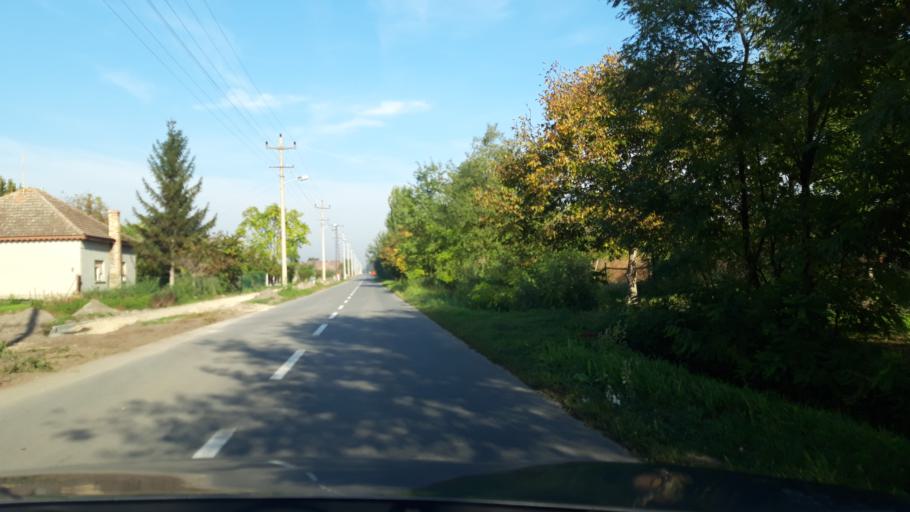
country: HU
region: Csongrad
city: Morahalom
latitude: 46.1342
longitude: 19.8525
